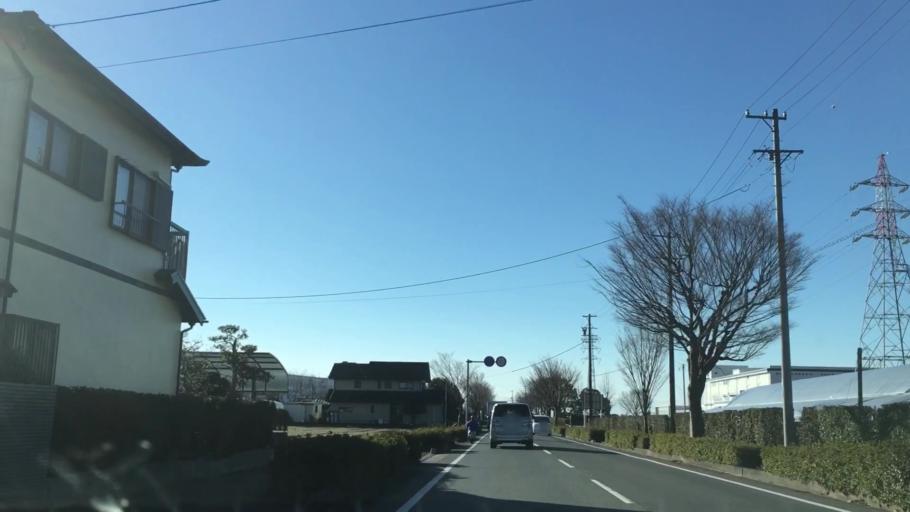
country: JP
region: Shizuoka
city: Hamakita
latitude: 34.8064
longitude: 137.7449
